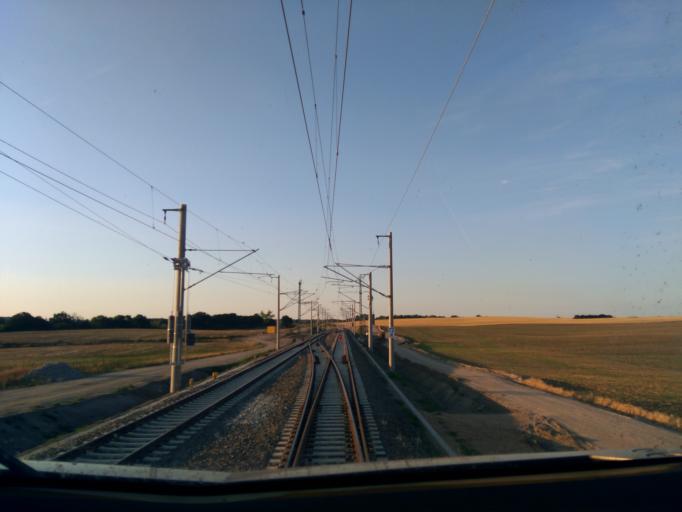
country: DE
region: Mecklenburg-Vorpommern
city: Seehof
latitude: 53.6871
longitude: 11.4106
